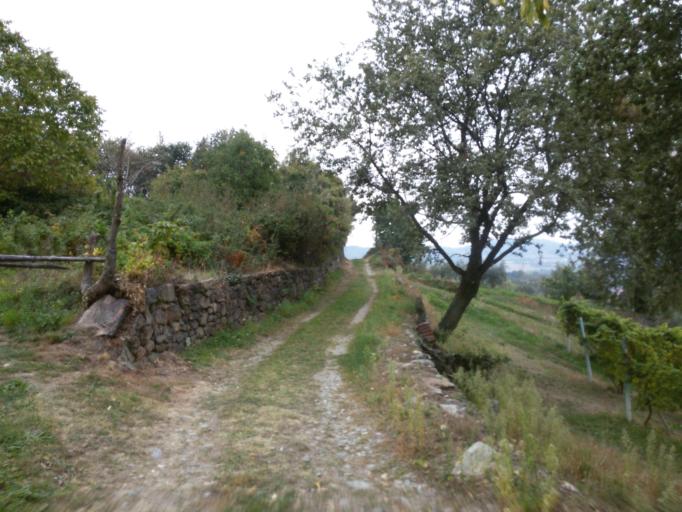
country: IT
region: Piedmont
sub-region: Provincia di Biella
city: Viverone
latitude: 45.4323
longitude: 8.0527
